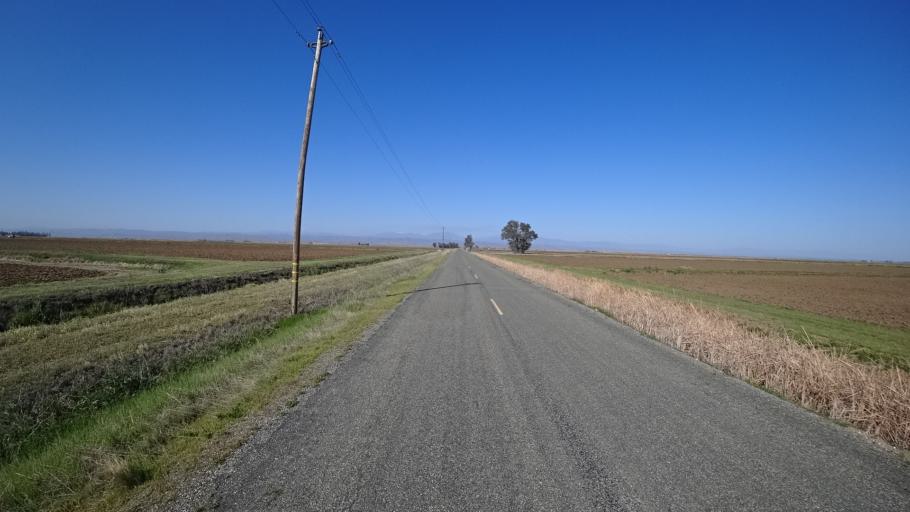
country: US
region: California
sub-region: Glenn County
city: Willows
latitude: 39.4509
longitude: -122.2041
